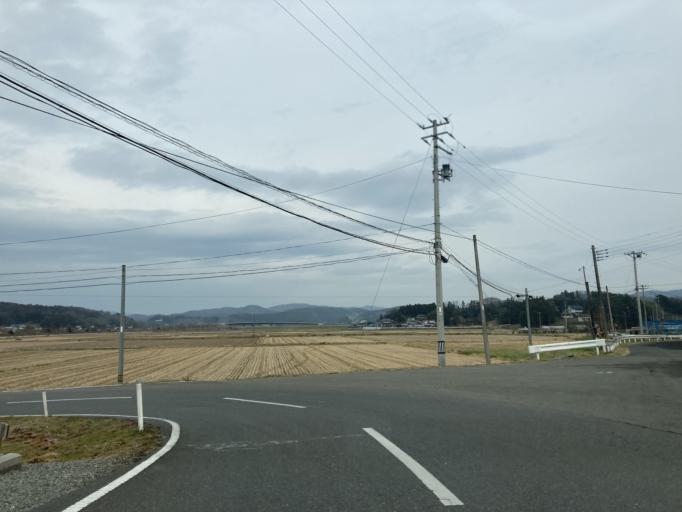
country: JP
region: Miyagi
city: Wakuya
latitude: 38.6885
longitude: 141.2770
